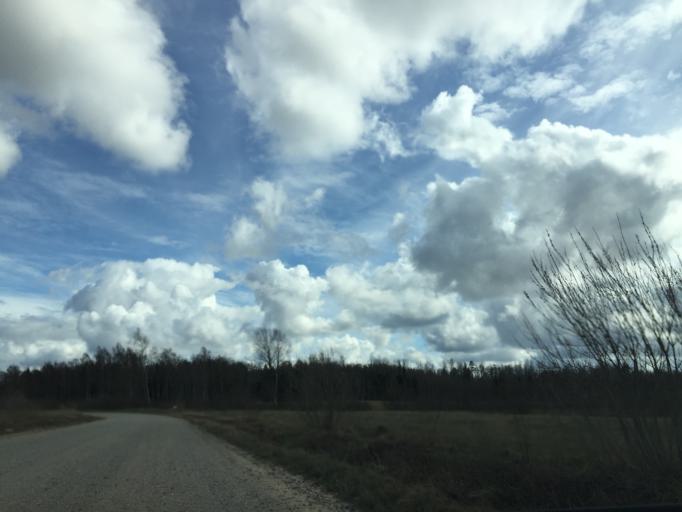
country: LV
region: Limbazu Rajons
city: Limbazi
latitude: 57.6100
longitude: 24.7854
